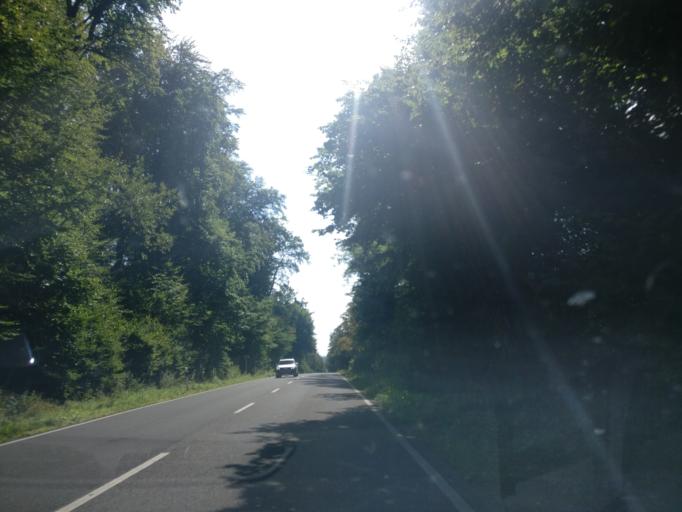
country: LU
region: Luxembourg
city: Bereldange
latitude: 49.6404
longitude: 6.1053
